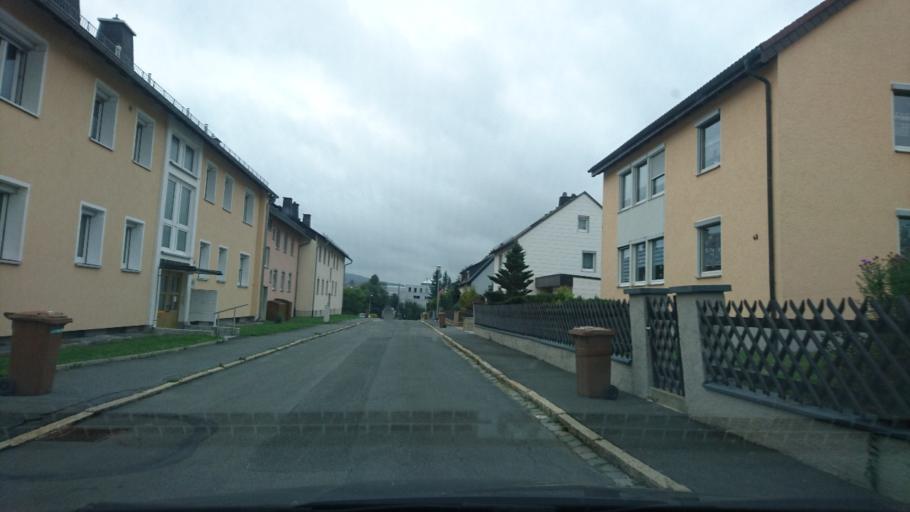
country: DE
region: Bavaria
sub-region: Upper Franconia
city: Naila
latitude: 50.3270
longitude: 11.7011
